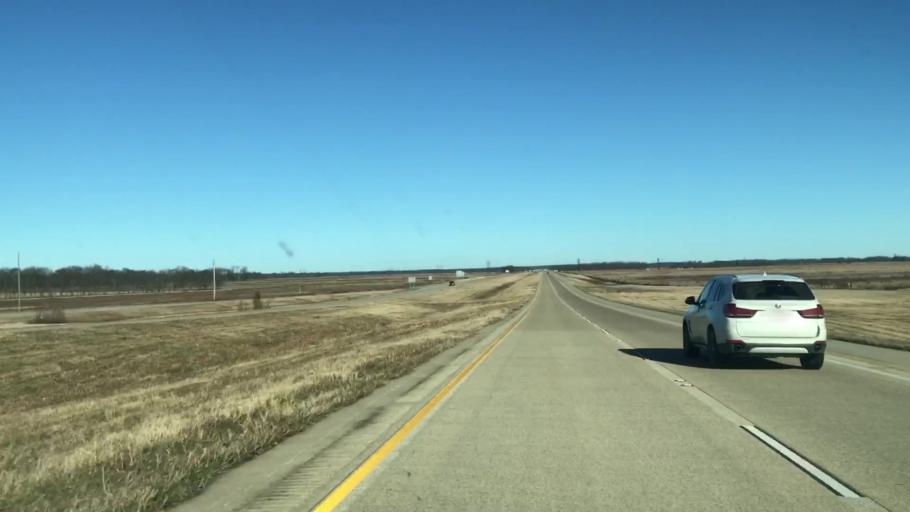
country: US
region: Louisiana
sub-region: Caddo Parish
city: Oil City
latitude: 32.7042
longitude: -93.8621
